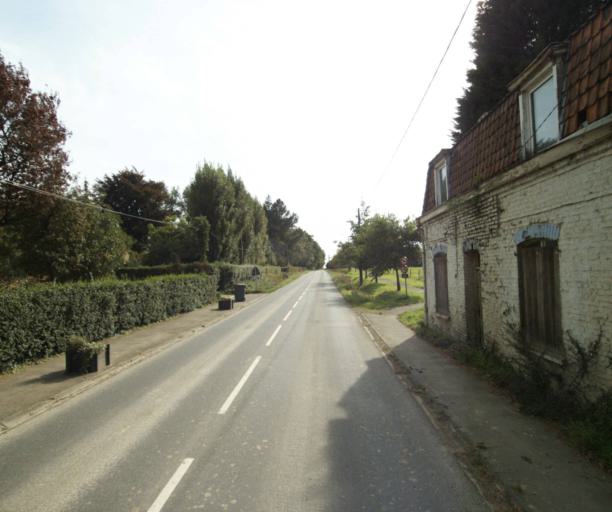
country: FR
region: Nord-Pas-de-Calais
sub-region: Departement du Nord
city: Radinghem-en-Weppes
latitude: 50.6161
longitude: 2.9094
